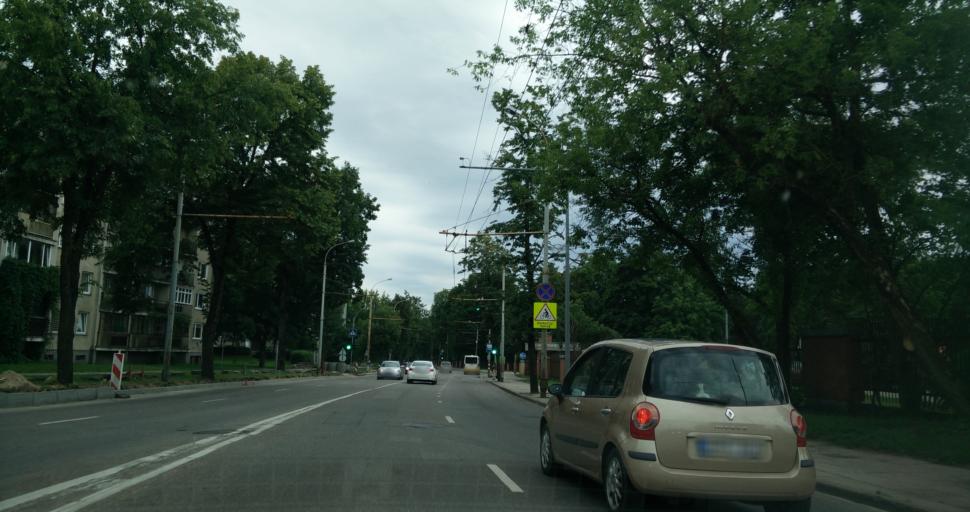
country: LT
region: Vilnius County
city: Rasos
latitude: 54.7210
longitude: 25.3180
